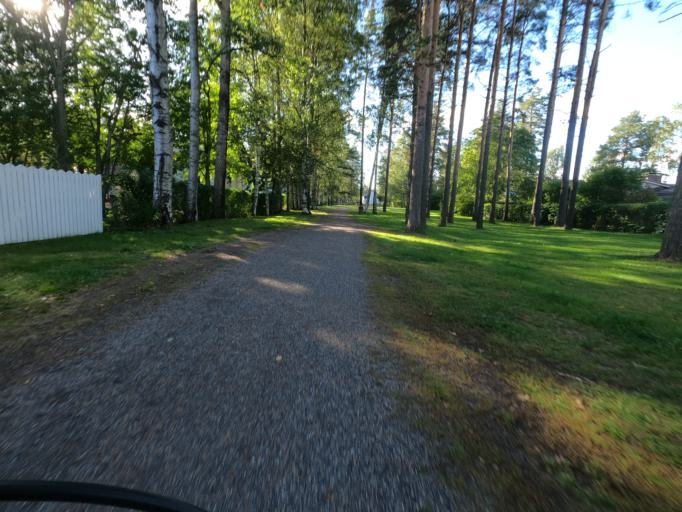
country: FI
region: North Karelia
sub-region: Joensuu
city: Joensuu
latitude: 62.6078
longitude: 29.7526
